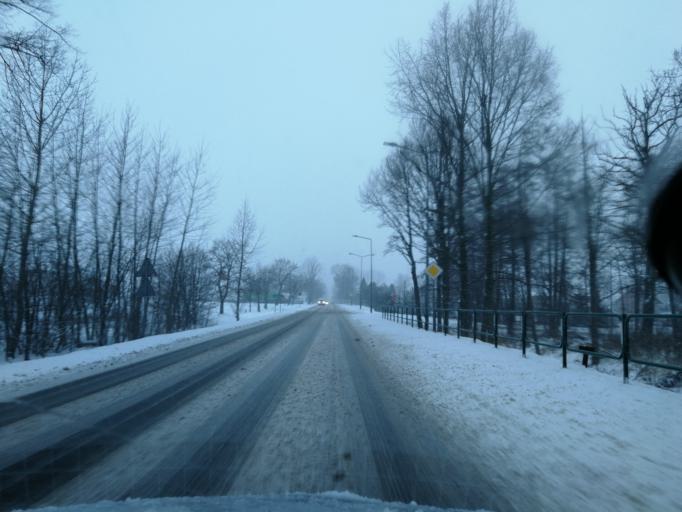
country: PL
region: Silesian Voivodeship
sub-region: Powiat pszczynski
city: Czarkow
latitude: 49.9888
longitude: 18.9180
